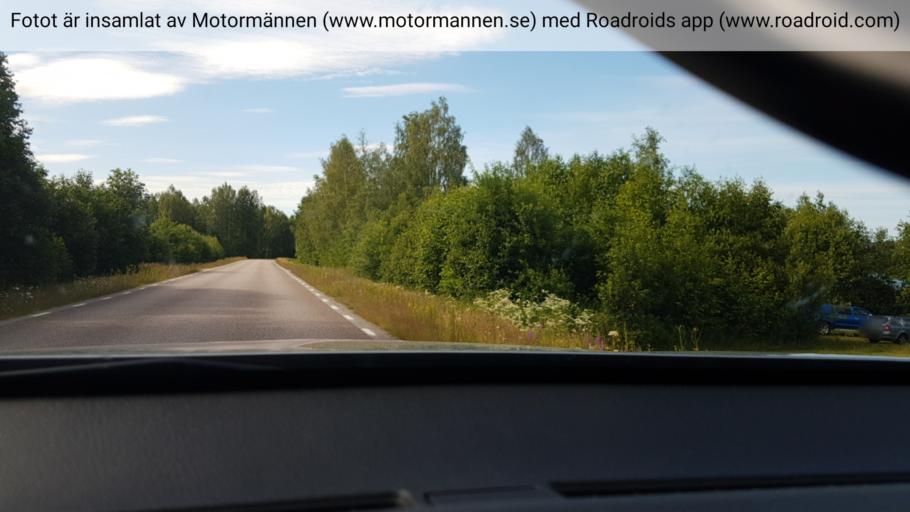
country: SE
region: Vaermland
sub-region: Hagfors Kommun
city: Hagfors
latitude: 60.0671
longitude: 13.5664
